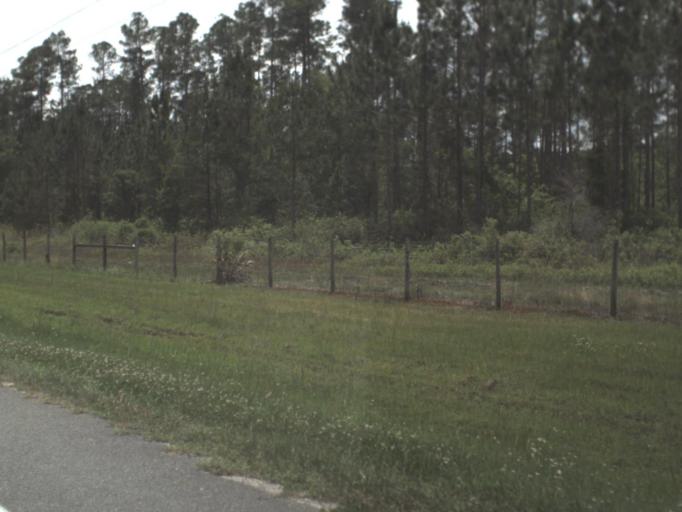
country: US
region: Florida
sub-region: Clay County
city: Asbury Lake
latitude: 29.9221
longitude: -81.8974
